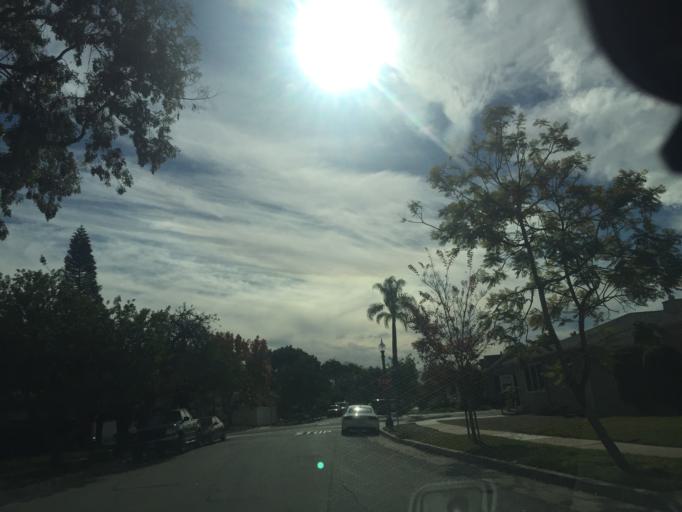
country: US
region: California
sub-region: San Diego County
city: Lemon Grove
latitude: 32.7634
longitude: -117.0858
